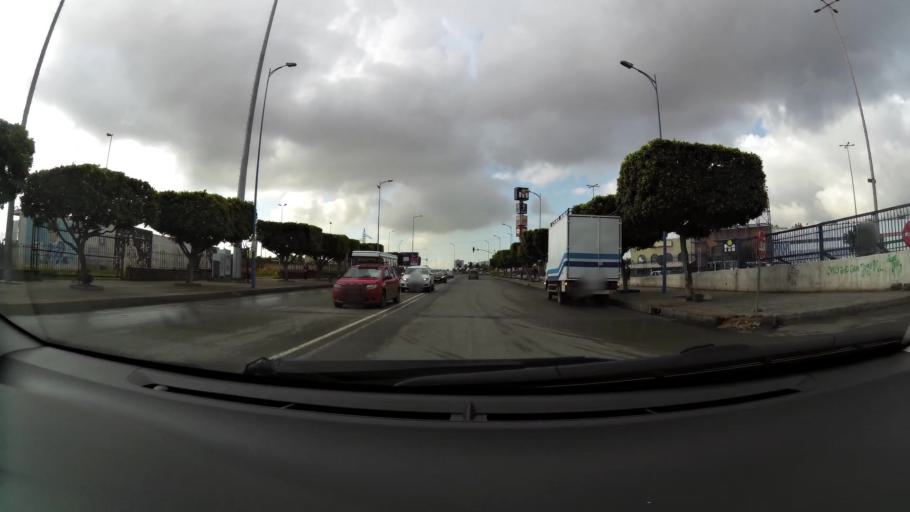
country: MA
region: Grand Casablanca
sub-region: Mediouna
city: Tit Mellil
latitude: 33.5961
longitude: -7.5303
